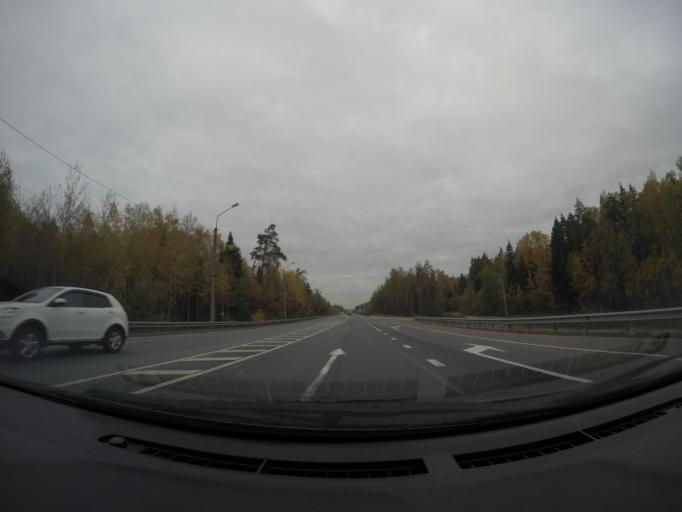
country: RU
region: Moskovskaya
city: Fryazevo
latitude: 55.7156
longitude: 38.4233
